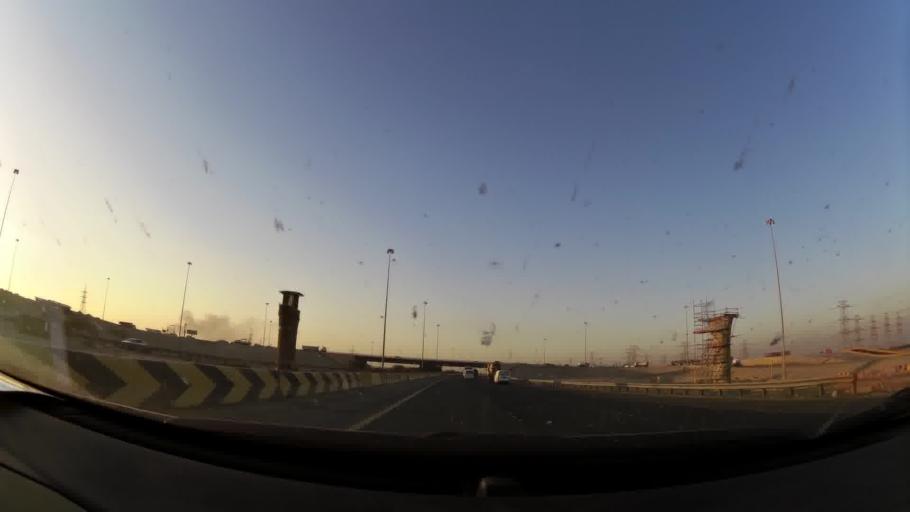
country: KW
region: Al Ahmadi
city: Al Fahahil
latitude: 28.9576
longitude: 48.1241
